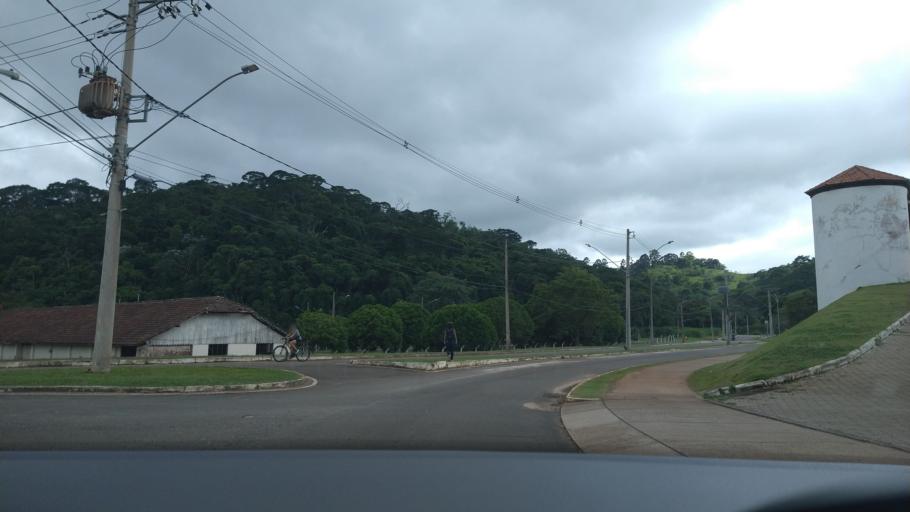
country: BR
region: Minas Gerais
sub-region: Vicosa
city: Vicosa
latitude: -20.7680
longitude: -42.8621
